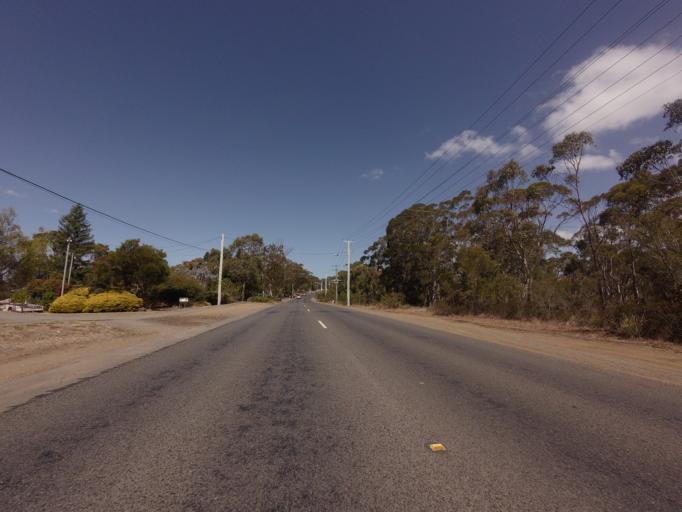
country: AU
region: Tasmania
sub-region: Hobart
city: Dynnyrne
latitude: -42.9150
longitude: 147.3161
